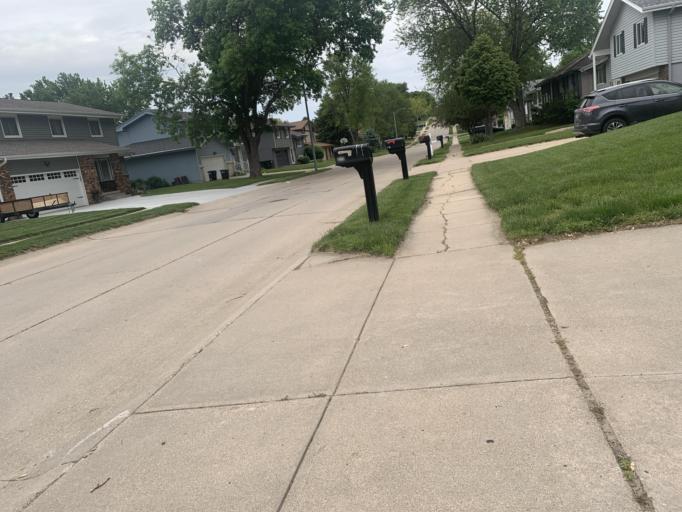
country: US
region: Nebraska
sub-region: Douglas County
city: Ralston
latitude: 41.1933
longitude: -96.0852
